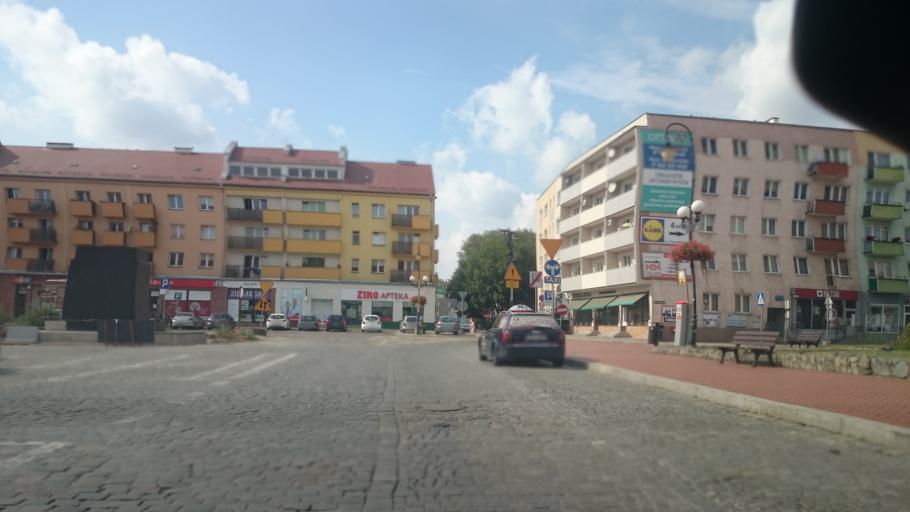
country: PL
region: Opole Voivodeship
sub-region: Powiat nyski
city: Nysa
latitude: 50.4740
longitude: 17.3337
